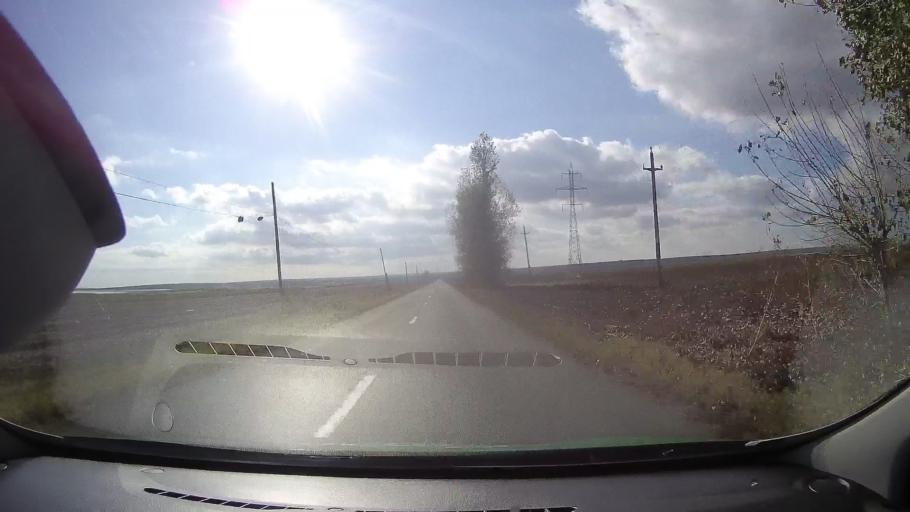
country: RO
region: Constanta
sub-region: Comuna Istria
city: Istria
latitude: 44.5421
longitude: 28.6903
